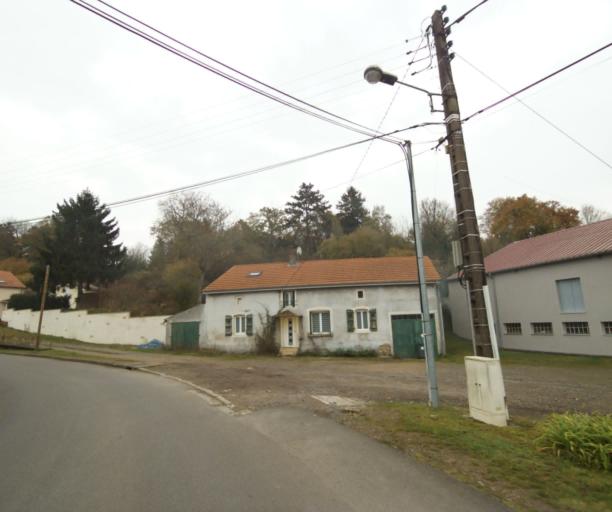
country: FR
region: Lorraine
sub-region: Departement de Meurthe-et-Moselle
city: Mancieulles
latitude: 49.2822
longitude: 5.8906
